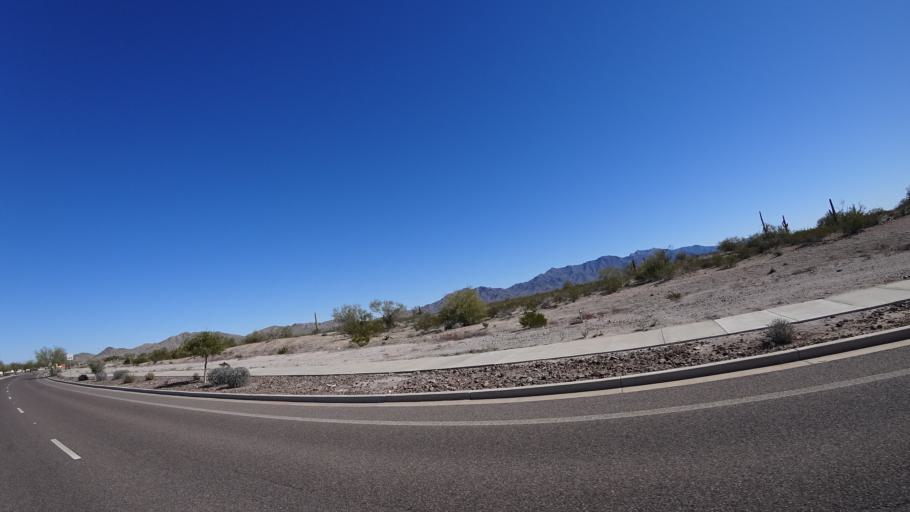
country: US
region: Arizona
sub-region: Maricopa County
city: Goodyear
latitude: 33.3153
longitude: -112.4331
